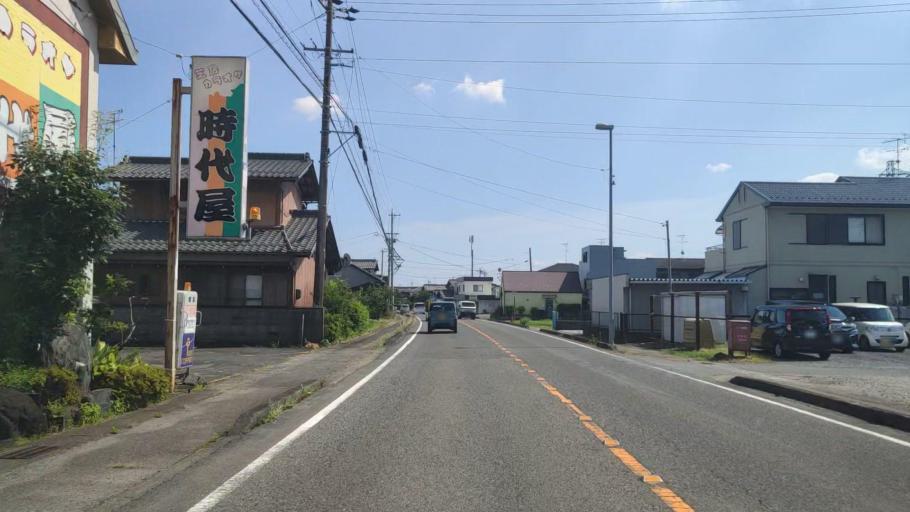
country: JP
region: Gifu
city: Godo
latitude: 35.4711
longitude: 136.6753
